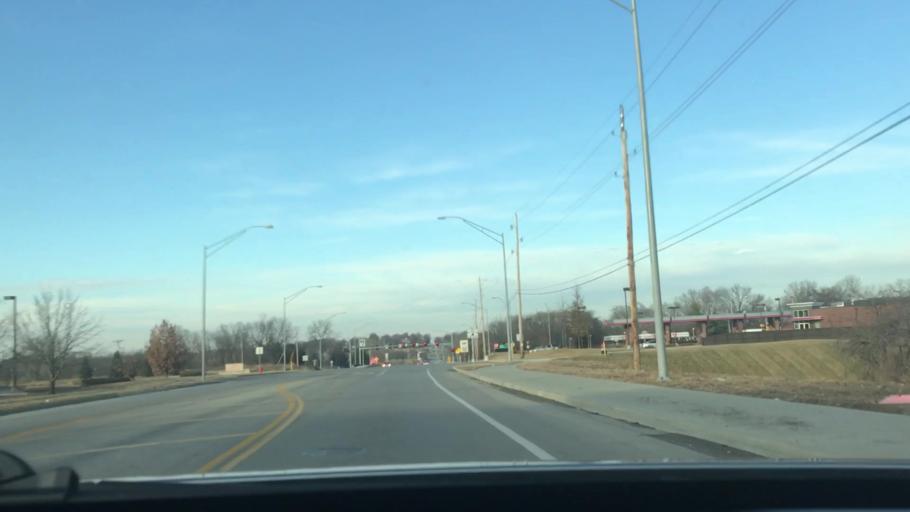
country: US
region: Missouri
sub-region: Jackson County
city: Independence
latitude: 39.0324
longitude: -94.3880
